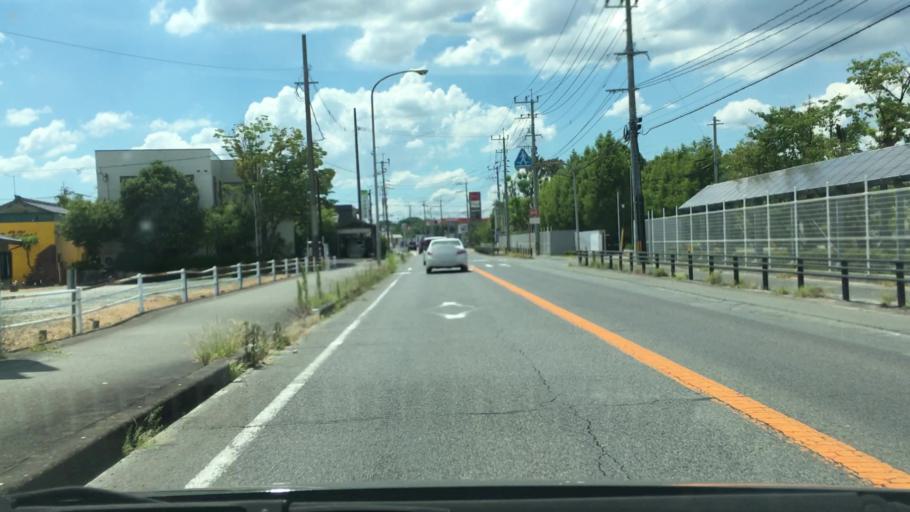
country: JP
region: Saga Prefecture
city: Tosu
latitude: 33.3521
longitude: 130.4660
